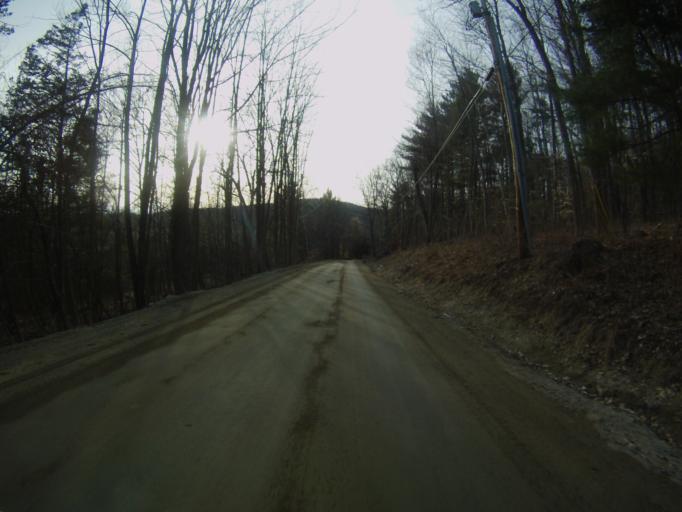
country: US
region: Vermont
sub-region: Addison County
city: Middlebury (village)
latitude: 44.0316
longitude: -73.2647
